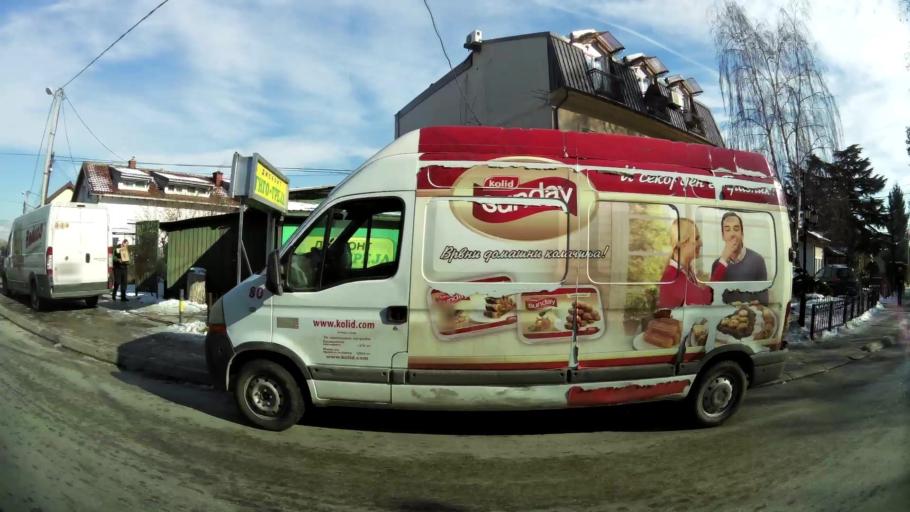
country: MK
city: Krushopek
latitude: 42.0063
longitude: 21.3653
